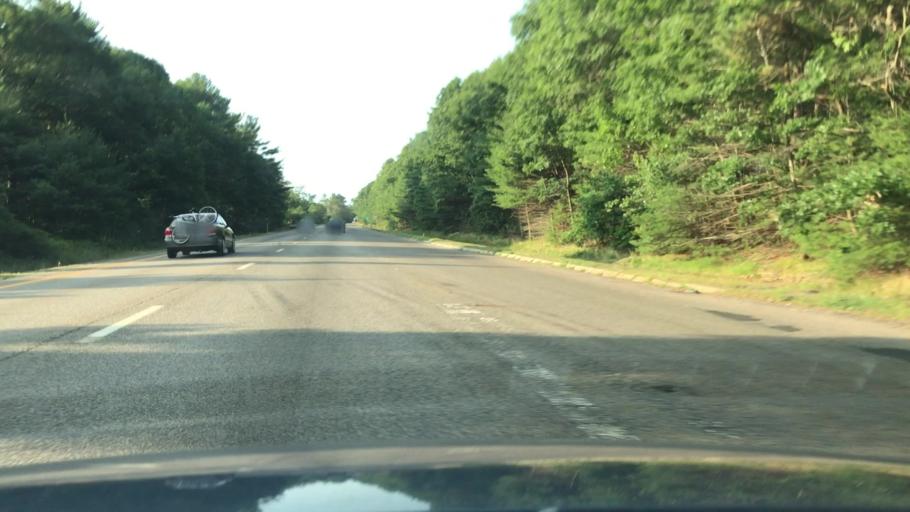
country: US
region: Massachusetts
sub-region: Plymouth County
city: Marshfield
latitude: 42.0526
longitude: -70.7248
